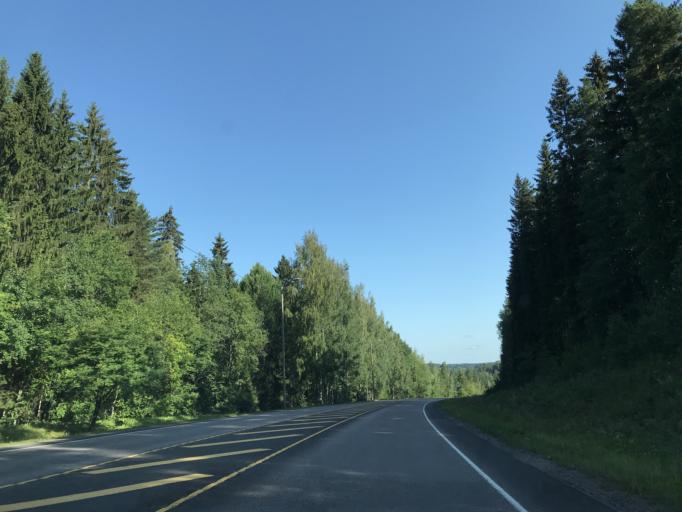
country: FI
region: Paijanne Tavastia
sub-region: Lahti
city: Lahti
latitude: 61.0436
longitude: 25.6648
